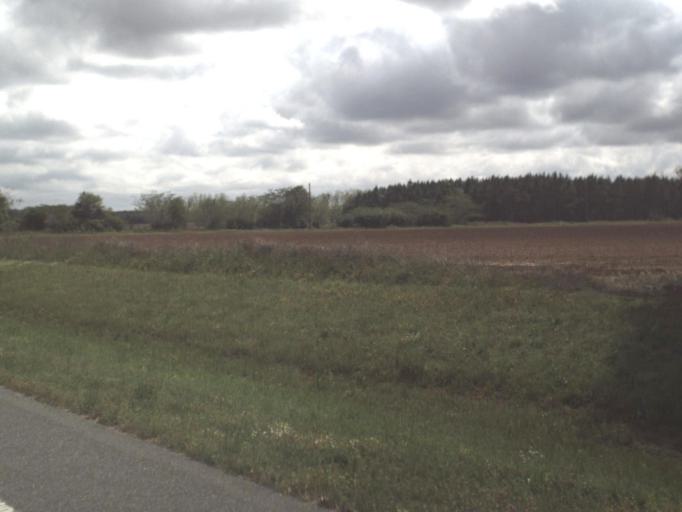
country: US
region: Florida
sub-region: Santa Rosa County
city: Point Baker
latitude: 30.7686
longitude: -87.0929
